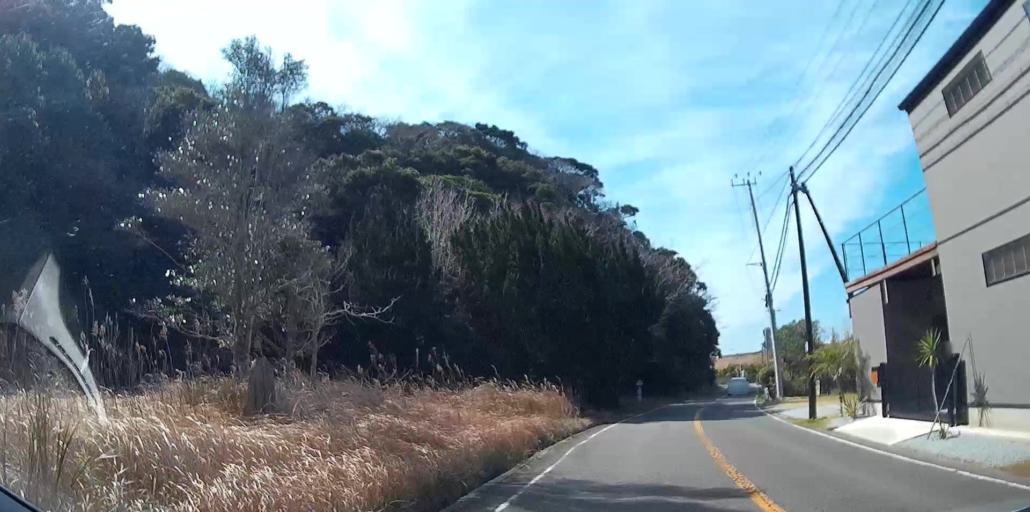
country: JP
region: Chiba
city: Tateyama
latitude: 34.9750
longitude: 139.7627
